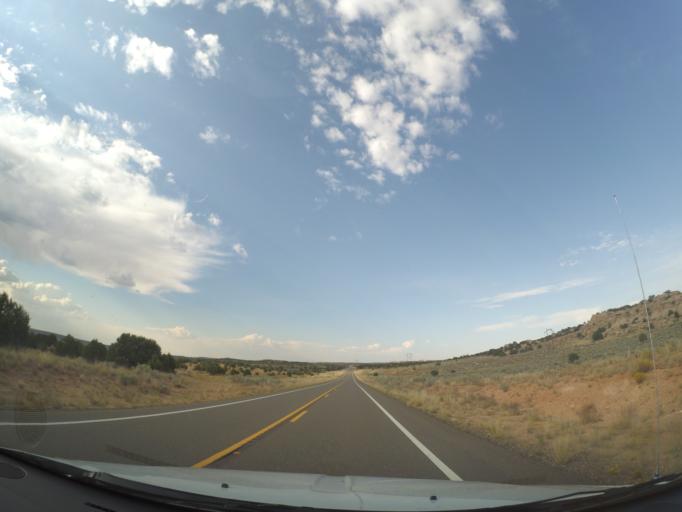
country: US
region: Arizona
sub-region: Coconino County
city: LeChee
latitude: 36.6404
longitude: -111.4407
